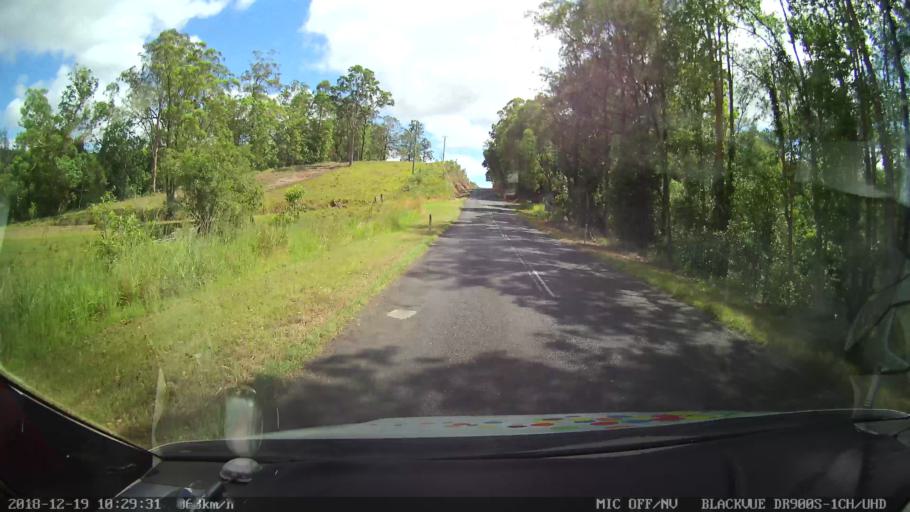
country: AU
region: New South Wales
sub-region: Lismore Municipality
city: Larnook
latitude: -28.5955
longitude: 153.1006
